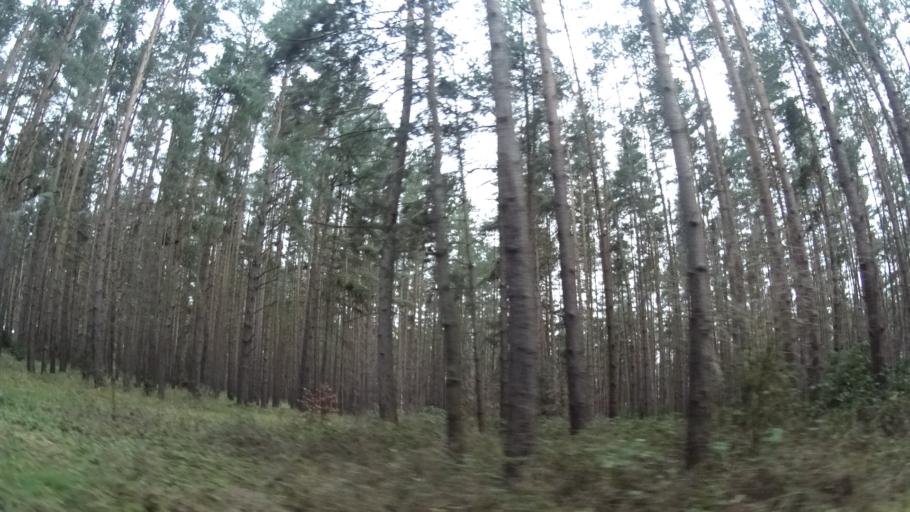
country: DE
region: Thuringia
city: Reinstadt
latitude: 50.7553
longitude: 11.4554
